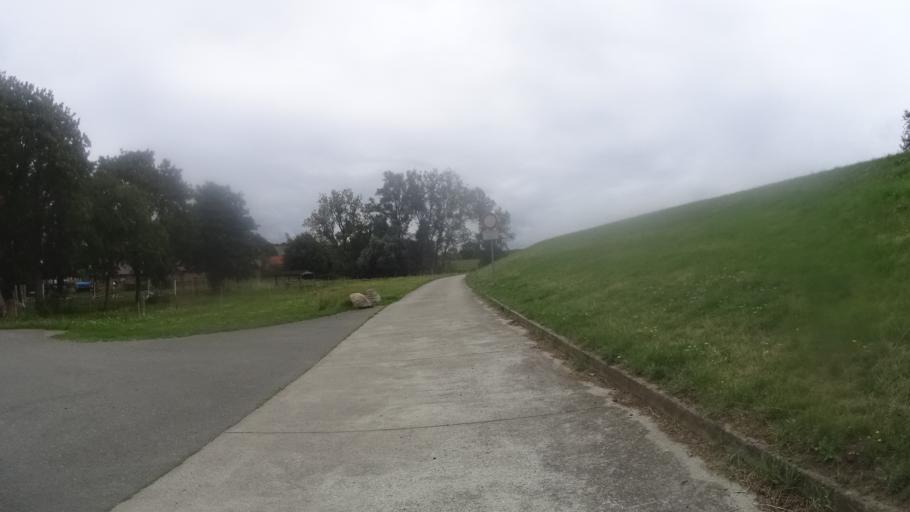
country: DE
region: Lower Saxony
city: Tosterglope
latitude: 53.2728
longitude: 10.8272
